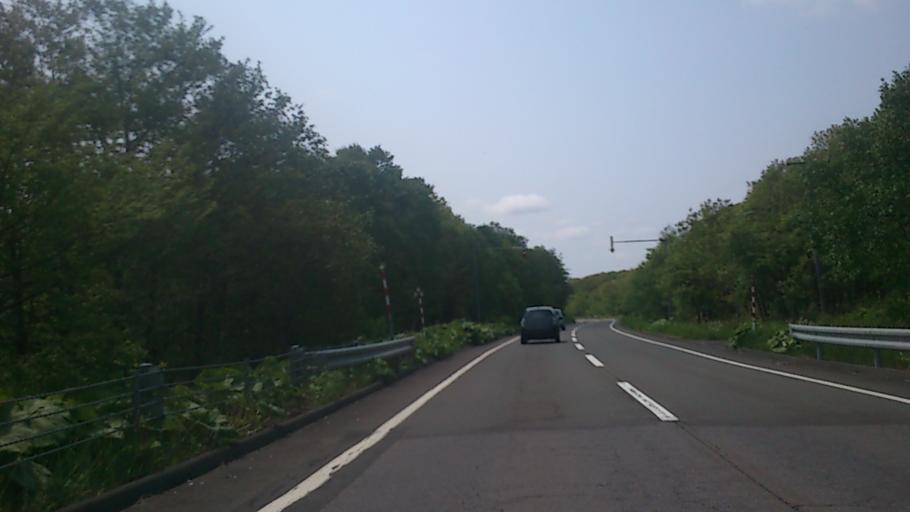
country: JP
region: Hokkaido
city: Shibetsu
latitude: 43.3078
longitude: 145.2137
